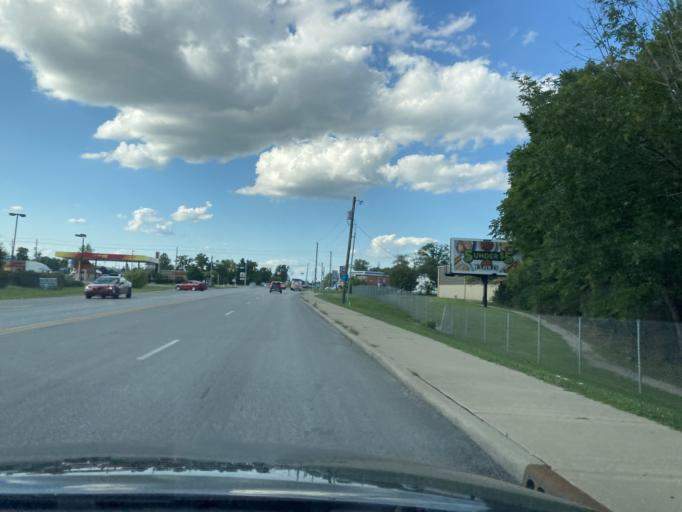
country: US
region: Indiana
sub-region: Boone County
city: Zionsville
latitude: 39.8803
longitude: -86.2443
